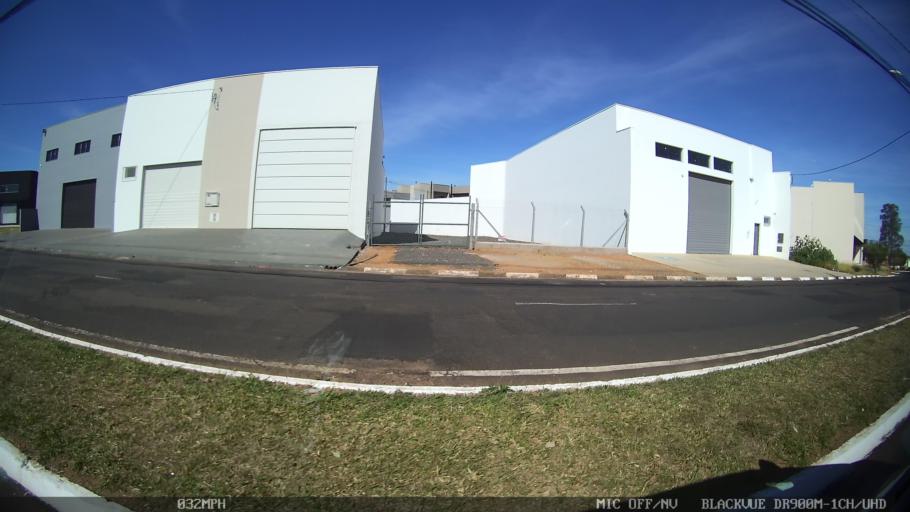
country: BR
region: Sao Paulo
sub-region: Franca
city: Franca
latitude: -20.5401
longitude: -47.3632
